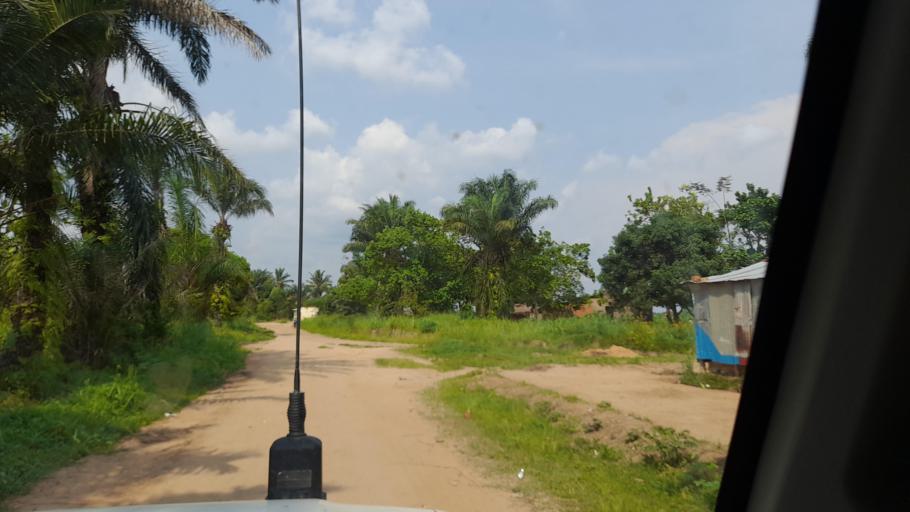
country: CD
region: Kasai-Occidental
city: Kananga
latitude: -5.9166
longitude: 22.4775
